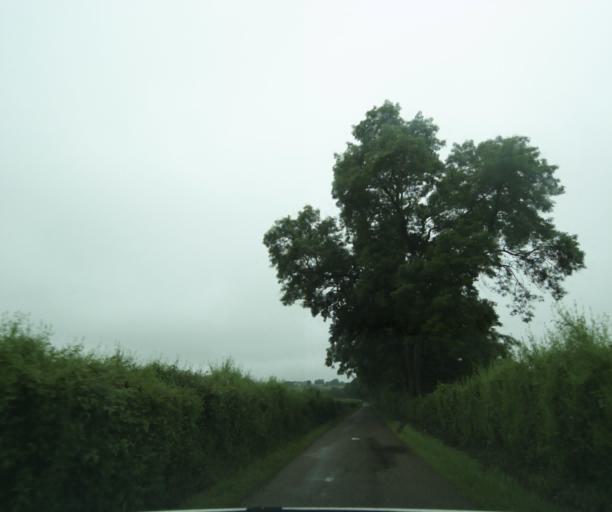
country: FR
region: Bourgogne
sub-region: Departement de Saone-et-Loire
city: Charolles
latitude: 46.3959
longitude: 4.1967
